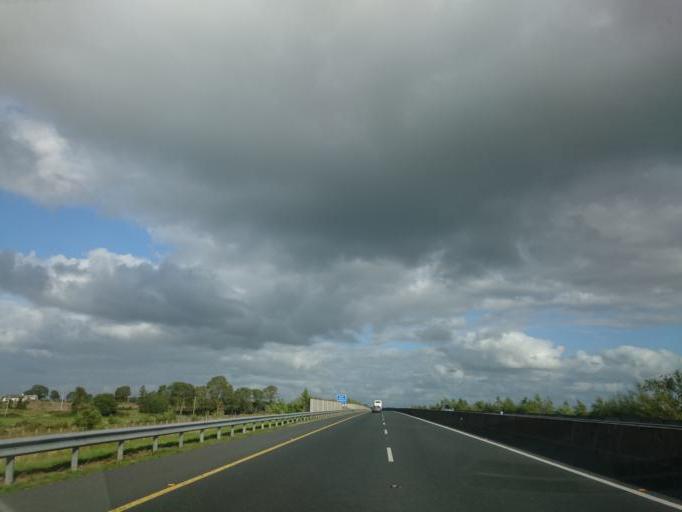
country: IE
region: Connaught
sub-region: County Galway
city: Athenry
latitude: 53.2721
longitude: -8.6790
